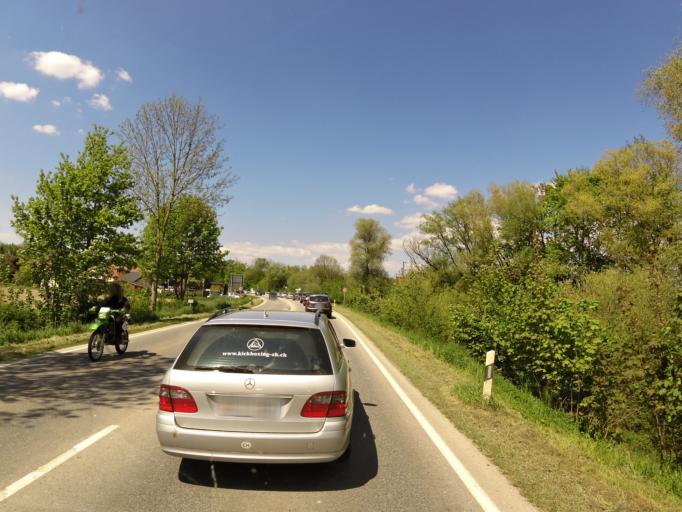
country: DE
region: Bavaria
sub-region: Lower Bavaria
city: Plattling
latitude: 48.7683
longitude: 12.8898
